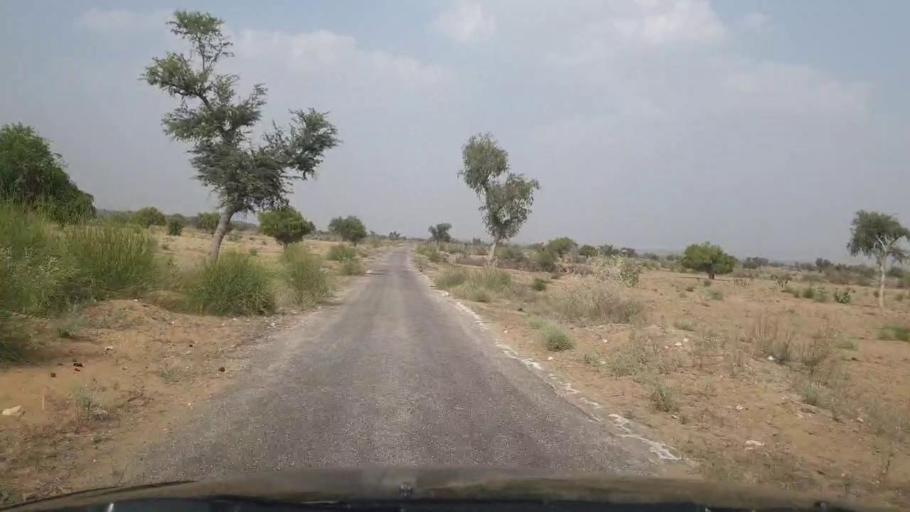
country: PK
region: Sindh
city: Islamkot
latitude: 24.8993
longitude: 70.5562
